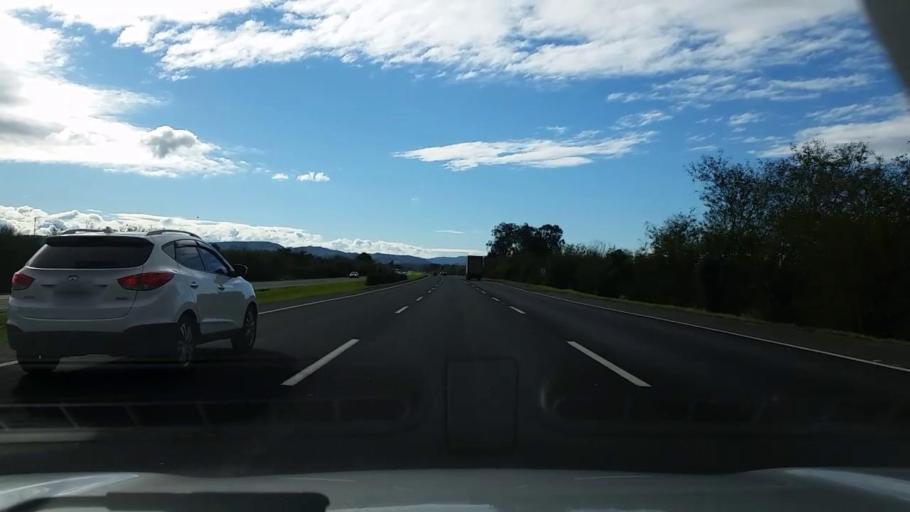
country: BR
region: Rio Grande do Sul
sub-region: Rolante
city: Rolante
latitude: -29.8832
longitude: -50.5371
